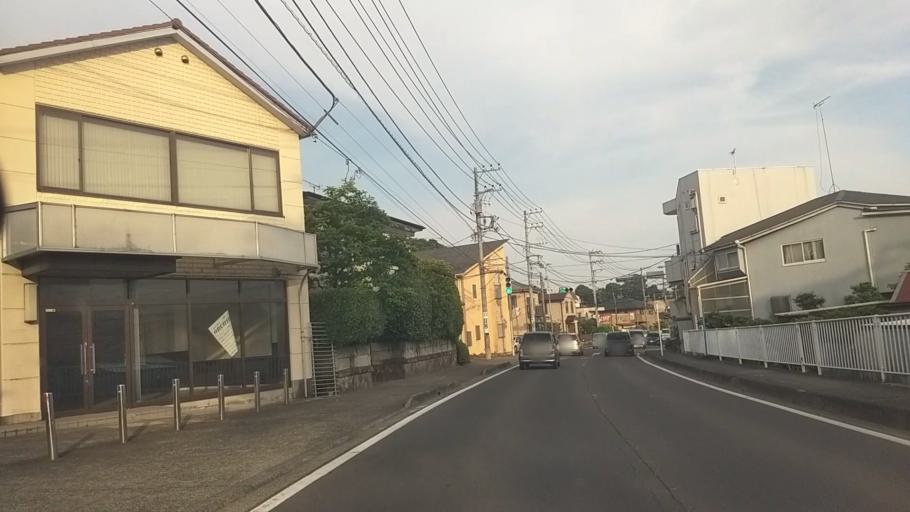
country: JP
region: Kanagawa
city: Odawara
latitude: 35.3105
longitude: 139.1203
